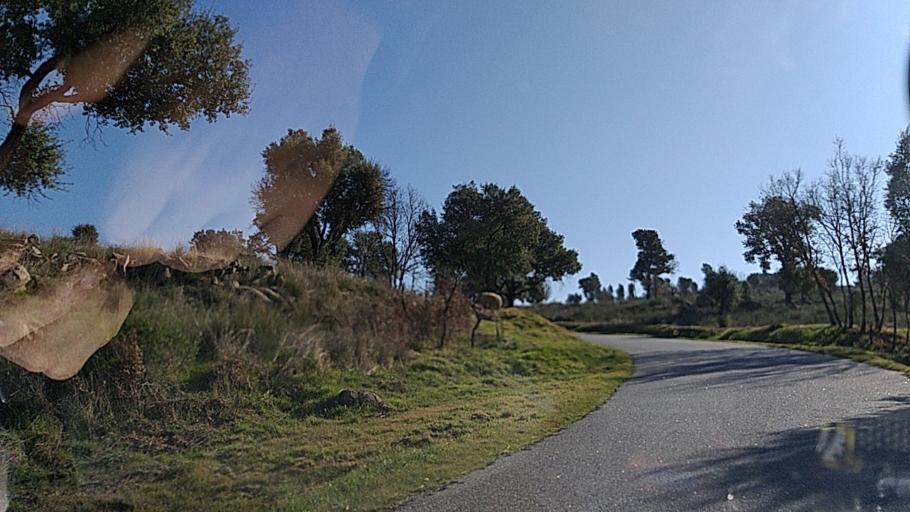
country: PT
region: Guarda
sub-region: Celorico da Beira
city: Celorico da Beira
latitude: 40.6931
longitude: -7.4483
